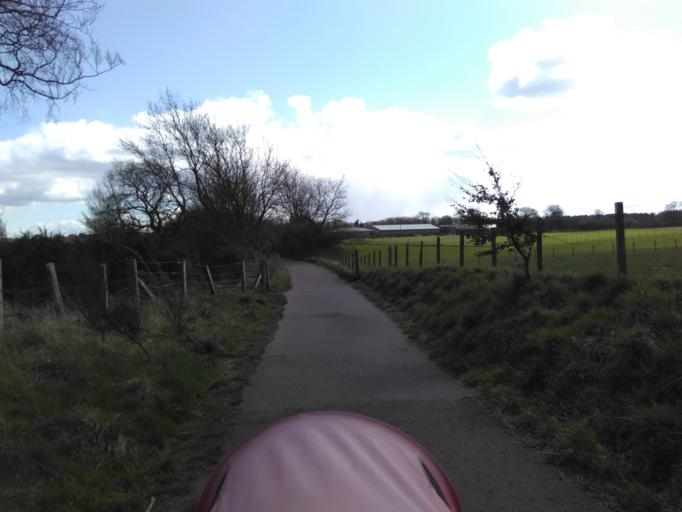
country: GB
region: Scotland
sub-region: Midlothian
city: Loanhead
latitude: 55.8670
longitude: -3.1516
